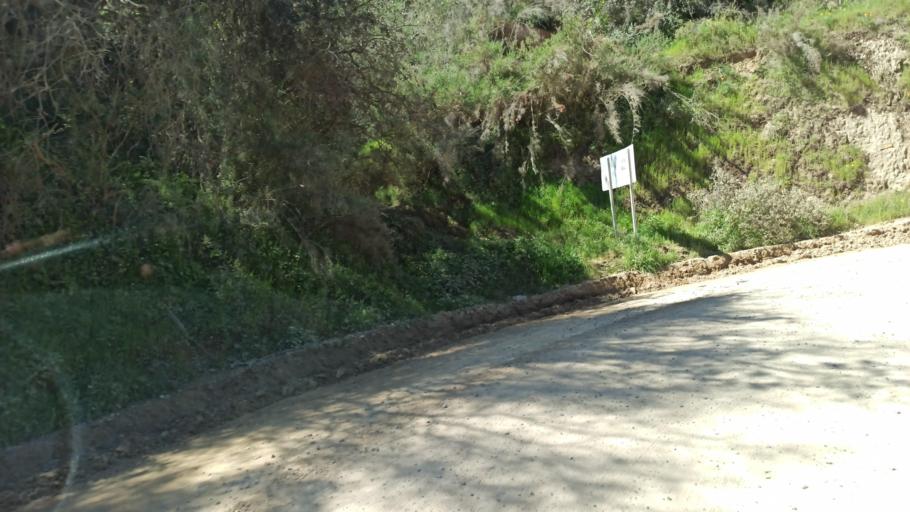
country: CL
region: Valparaiso
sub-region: Provincia de Marga Marga
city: Limache
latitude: -33.1996
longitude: -71.2623
